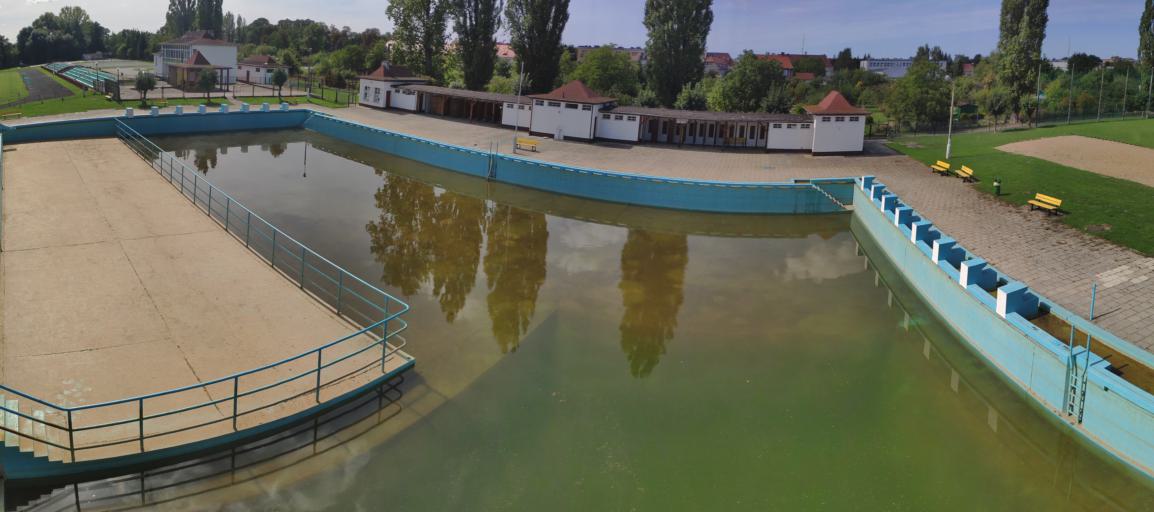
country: PL
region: Lubusz
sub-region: Powiat wschowski
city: Wschowa
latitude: 51.7971
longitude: 16.3192
